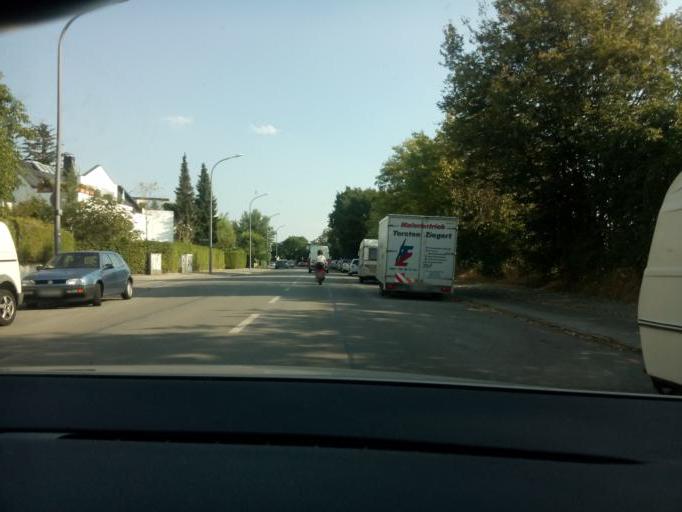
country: DE
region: Bavaria
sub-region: Upper Bavaria
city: Unterhaching
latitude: 48.0993
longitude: 11.6070
